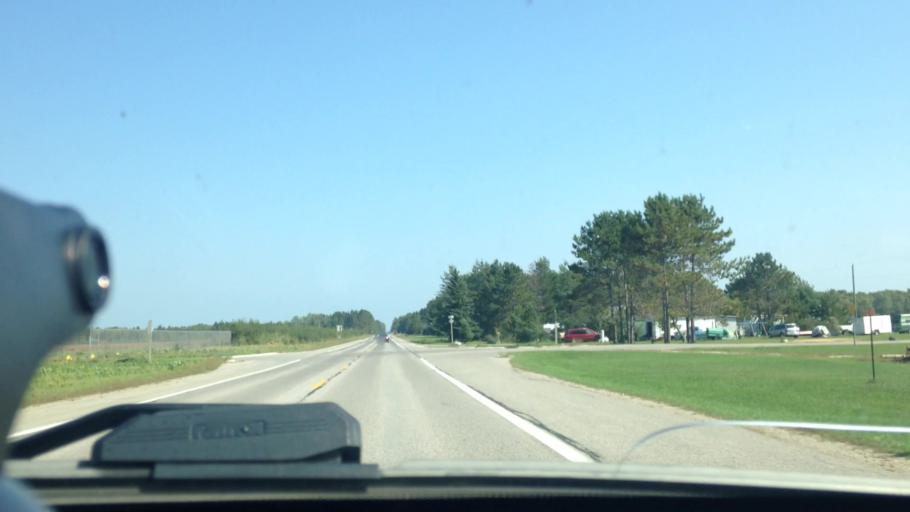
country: US
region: Michigan
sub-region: Luce County
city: Newberry
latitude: 46.3035
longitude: -85.4584
